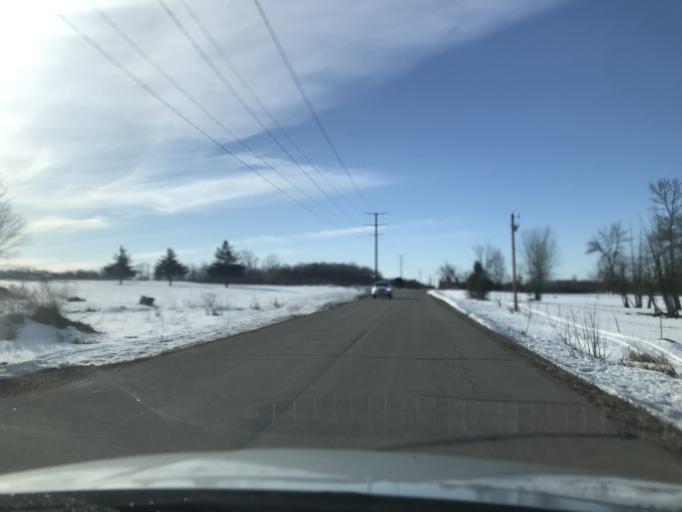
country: US
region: Wisconsin
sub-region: Oconto County
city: Oconto Falls
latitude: 44.9276
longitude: -88.0162
